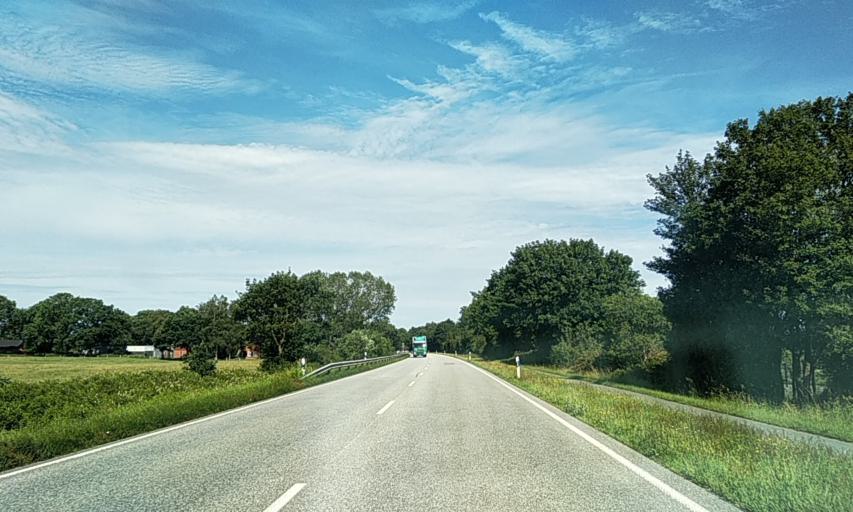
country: DE
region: Schleswig-Holstein
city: Fockbek
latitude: 54.3369
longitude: 9.6126
